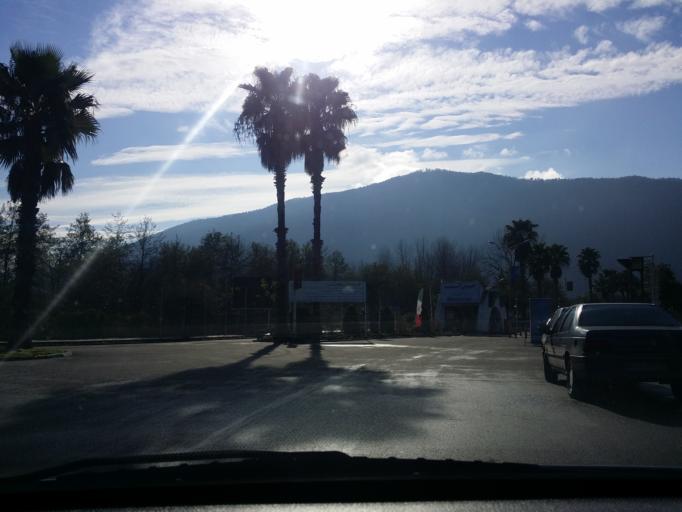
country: IR
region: Mazandaran
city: Chalus
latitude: 36.6871
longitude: 51.3060
